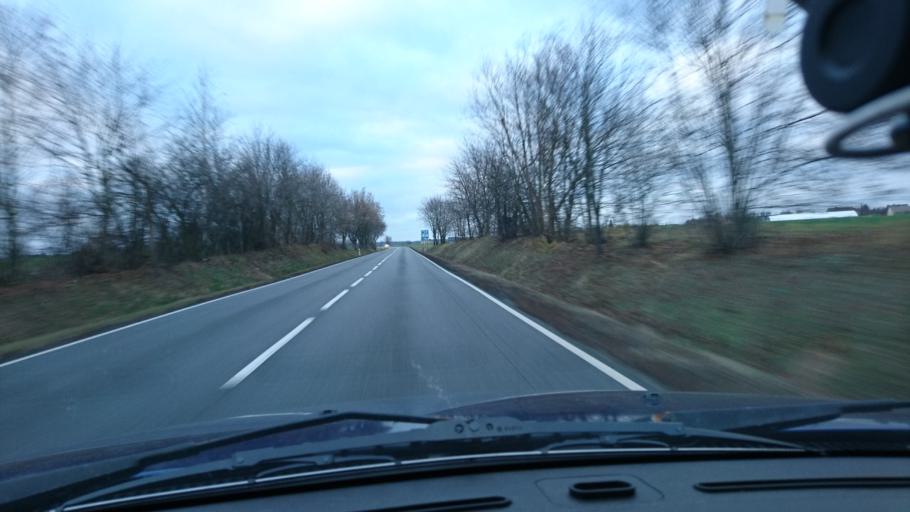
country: PL
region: Greater Poland Voivodeship
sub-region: Powiat kepinski
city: Opatow
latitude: 51.2159
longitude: 18.1405
